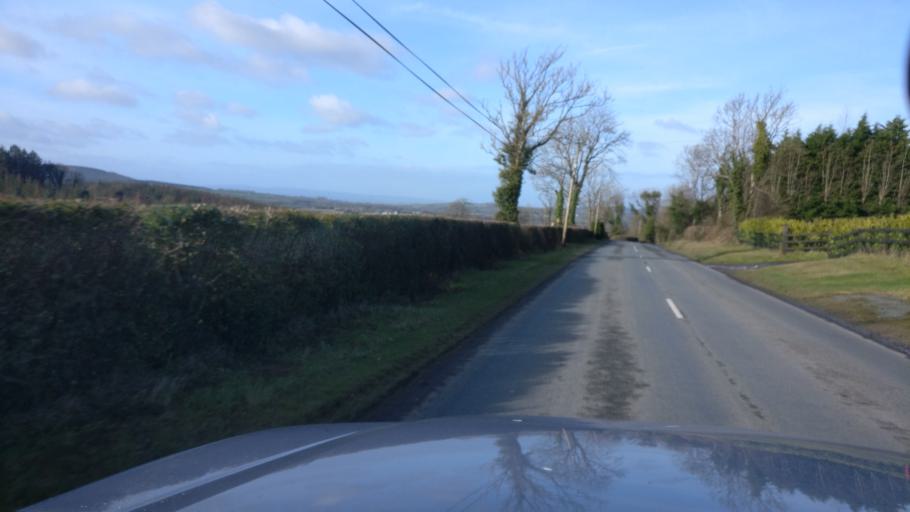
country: IE
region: Leinster
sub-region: Laois
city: Stradbally
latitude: 52.9381
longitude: -7.1975
